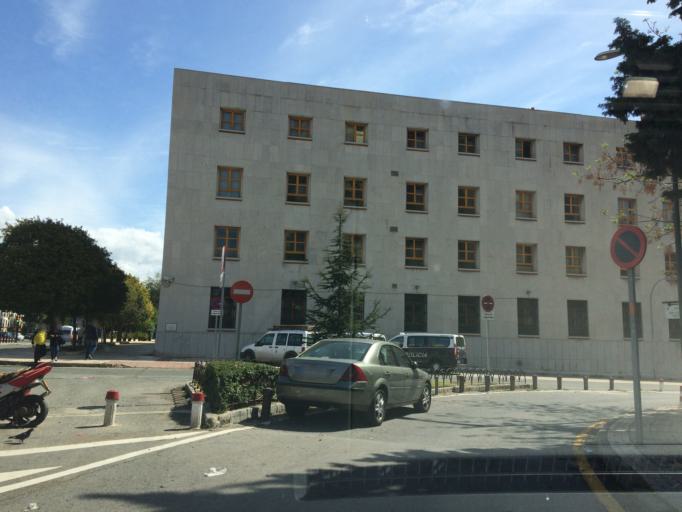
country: ES
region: Andalusia
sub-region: Provincia de Malaga
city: Malaga
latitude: 36.7145
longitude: -4.4496
